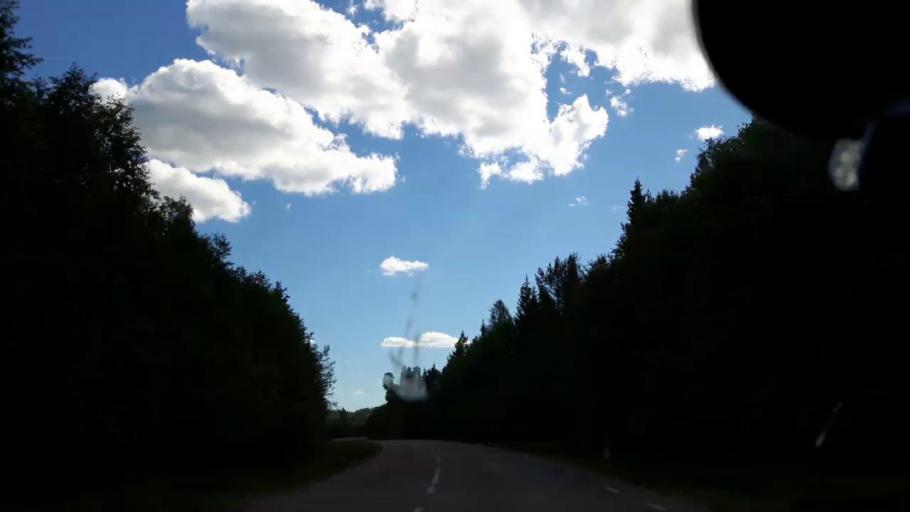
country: SE
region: Jaemtland
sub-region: Ragunda Kommun
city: Hammarstrand
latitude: 62.8433
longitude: 16.1726
